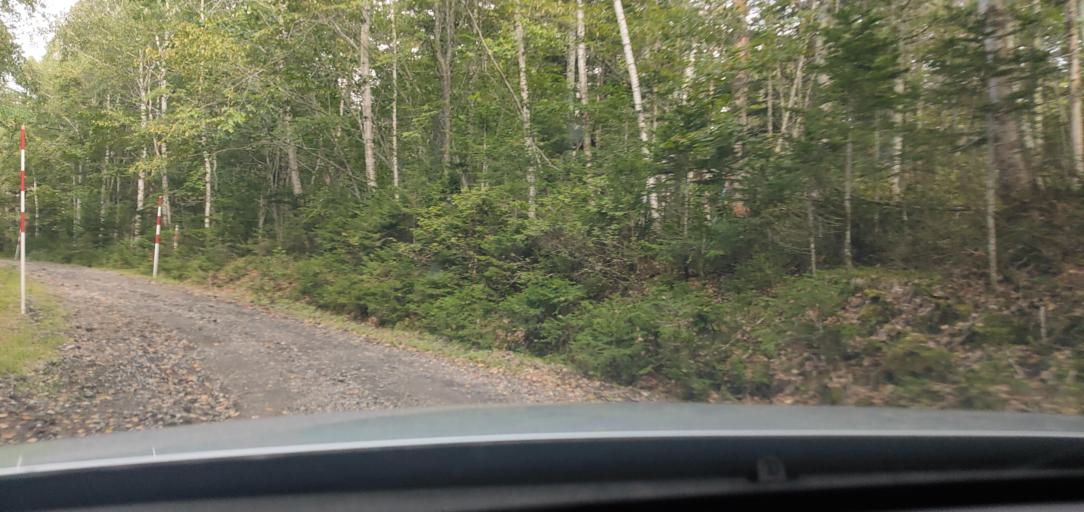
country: JP
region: Hokkaido
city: Kitami
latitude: 43.3727
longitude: 143.9636
